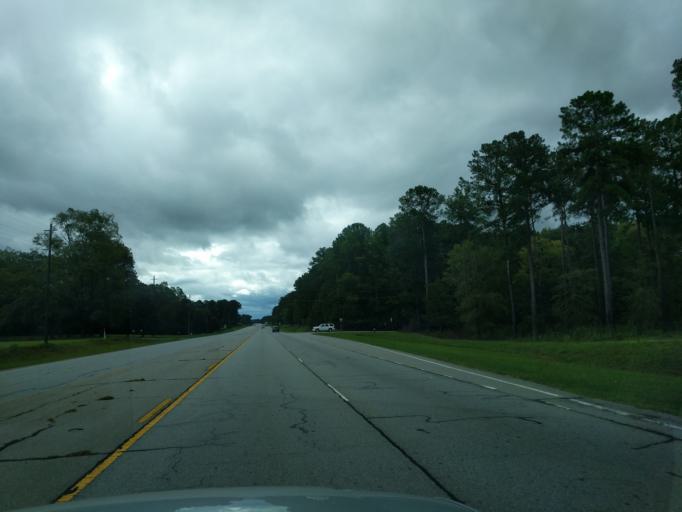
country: US
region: Georgia
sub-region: Wilkes County
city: Washington
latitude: 33.7193
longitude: -82.7072
